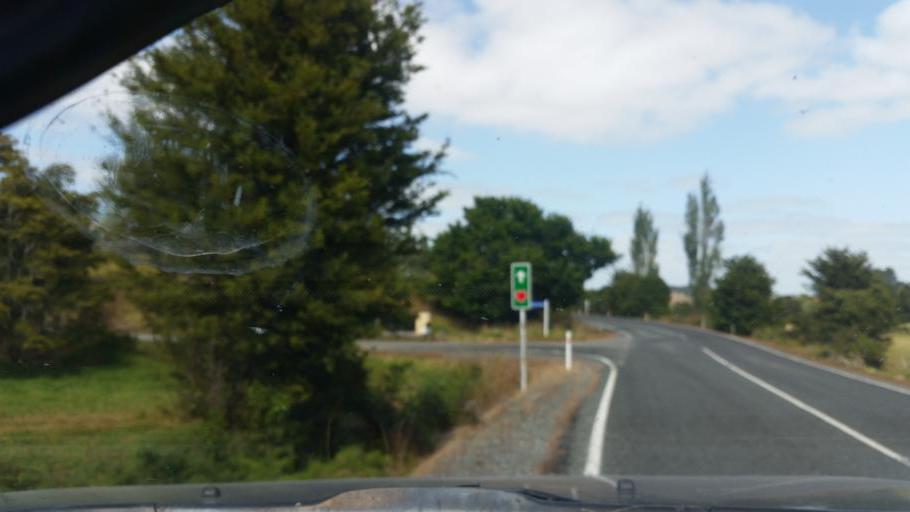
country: NZ
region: Northland
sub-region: Whangarei
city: Ruakaka
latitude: -35.9422
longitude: 174.2925
